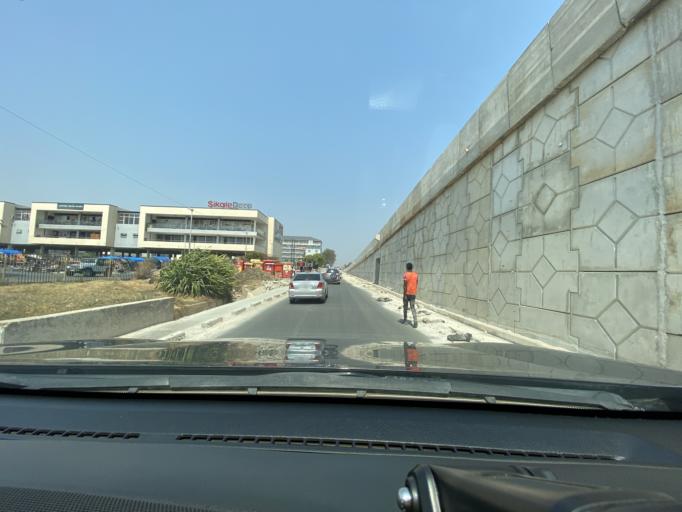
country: ZM
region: Lusaka
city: Lusaka
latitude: -15.3910
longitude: 28.3167
